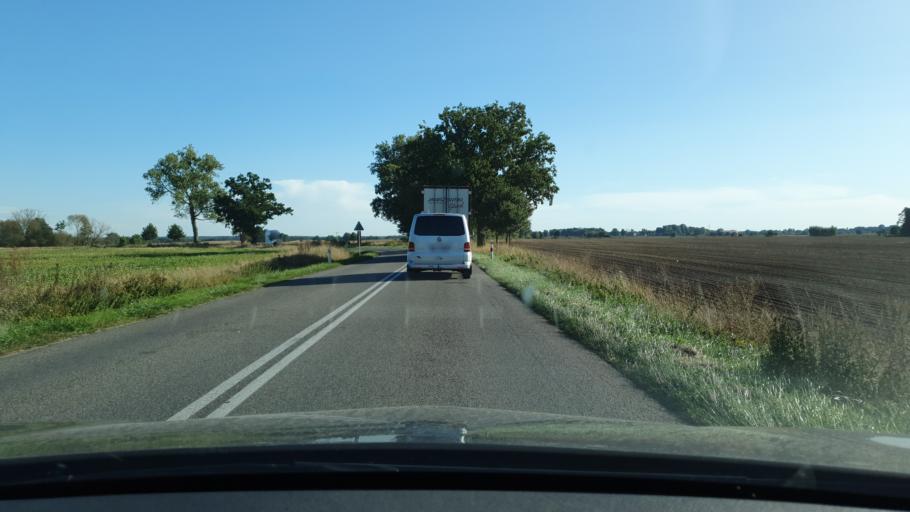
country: PL
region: West Pomeranian Voivodeship
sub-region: Powiat kamienski
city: Golczewo
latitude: 53.8259
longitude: 14.9299
